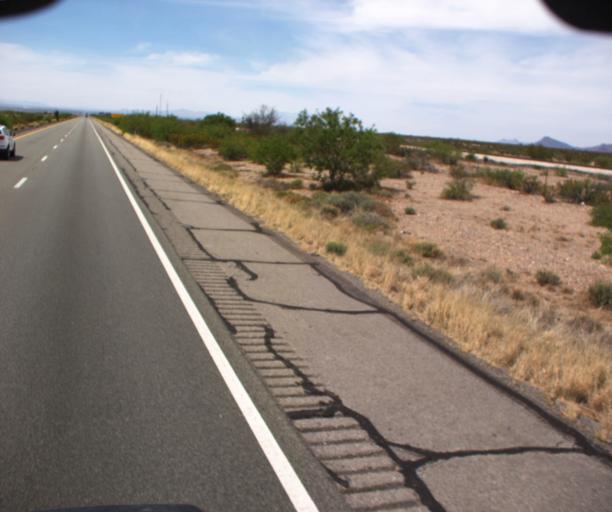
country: US
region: New Mexico
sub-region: Hidalgo County
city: Lordsburg
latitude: 32.2423
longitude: -109.1120
